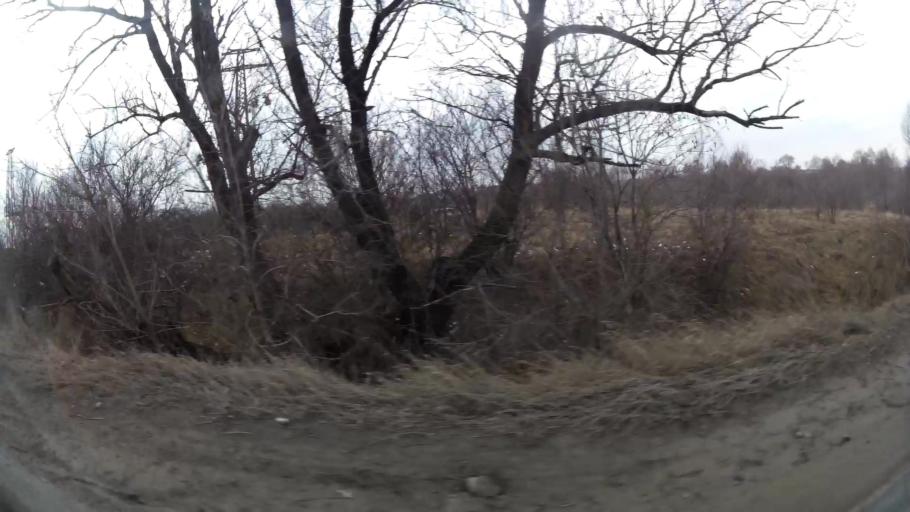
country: BG
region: Sofiya
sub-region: Obshtina Bozhurishte
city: Bozhurishte
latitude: 42.7002
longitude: 23.2303
